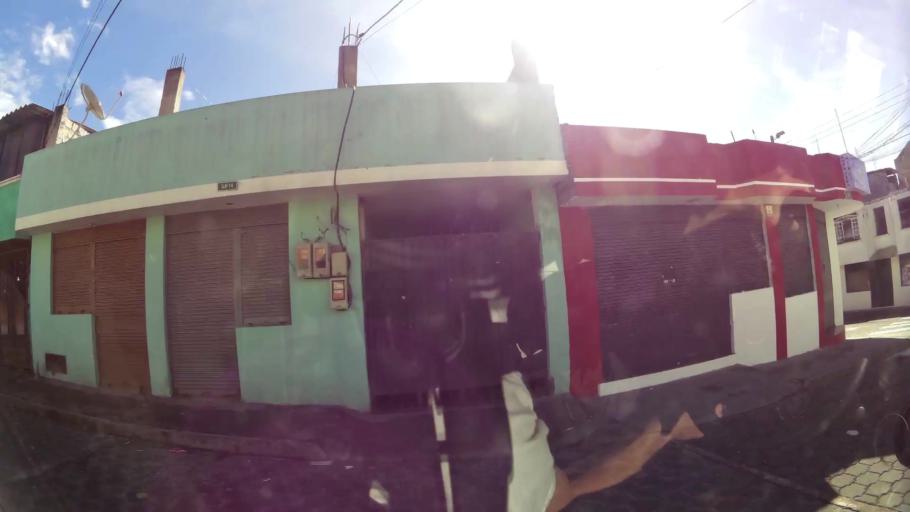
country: EC
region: Pichincha
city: Quito
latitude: -0.2999
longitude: -78.5648
